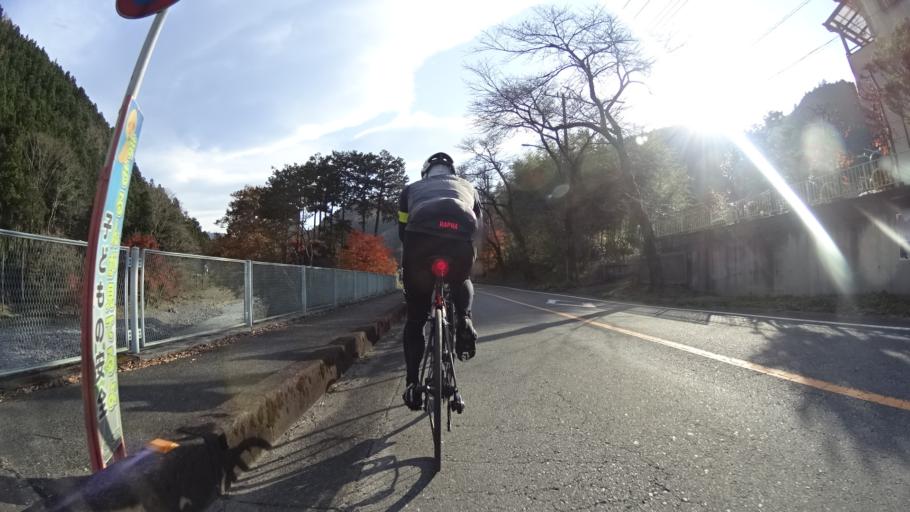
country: JP
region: Tokyo
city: Ome
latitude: 35.8641
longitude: 139.1869
